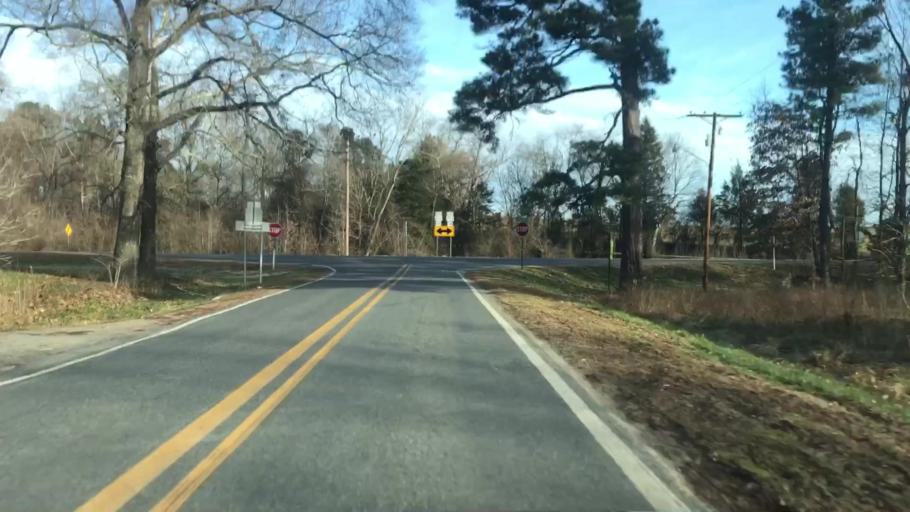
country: US
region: Arkansas
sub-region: Garland County
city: Rockwell
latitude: 34.5103
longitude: -93.2760
